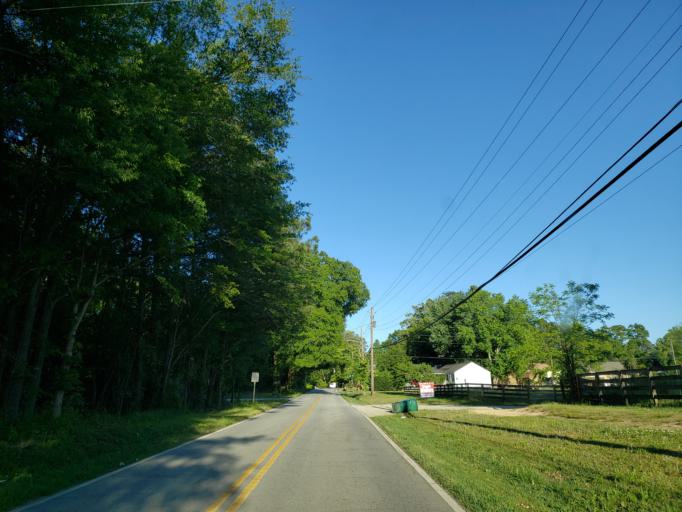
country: US
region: Georgia
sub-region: Haralson County
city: Tallapoosa
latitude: 33.7548
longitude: -85.3032
